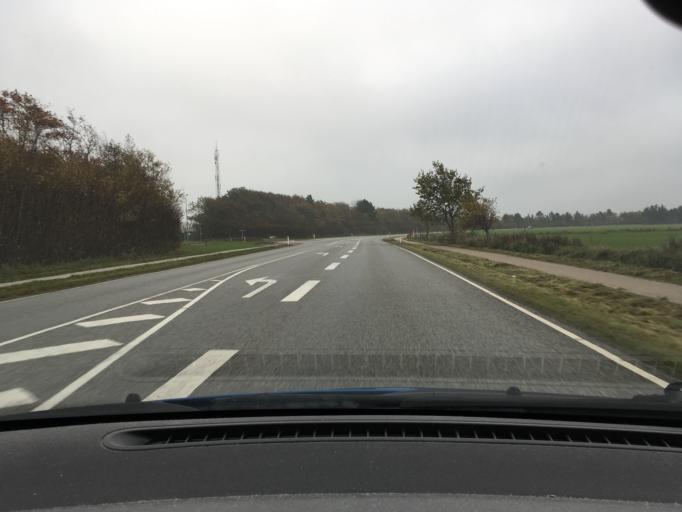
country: DK
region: South Denmark
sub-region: Tonder Kommune
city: Tonder
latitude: 54.9307
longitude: 8.8485
